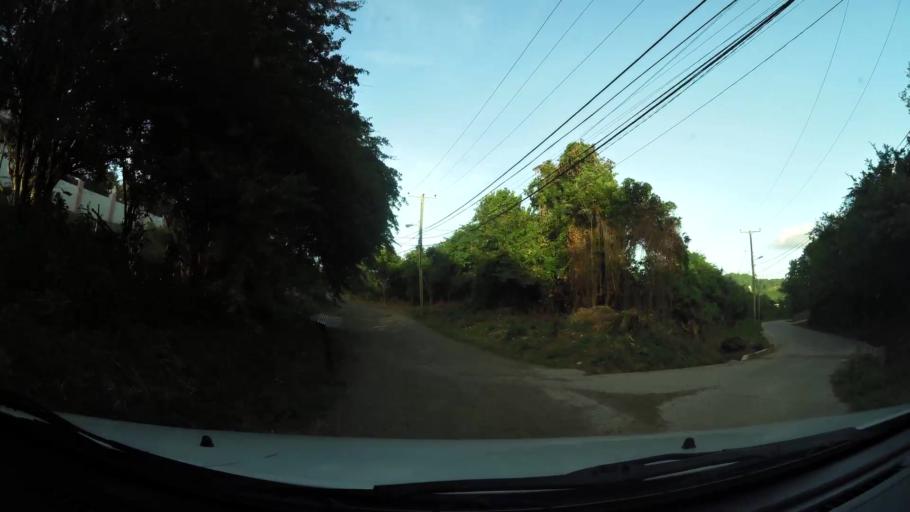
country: LC
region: Gros-Islet
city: Gros Islet
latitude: 14.0701
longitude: -60.9379
